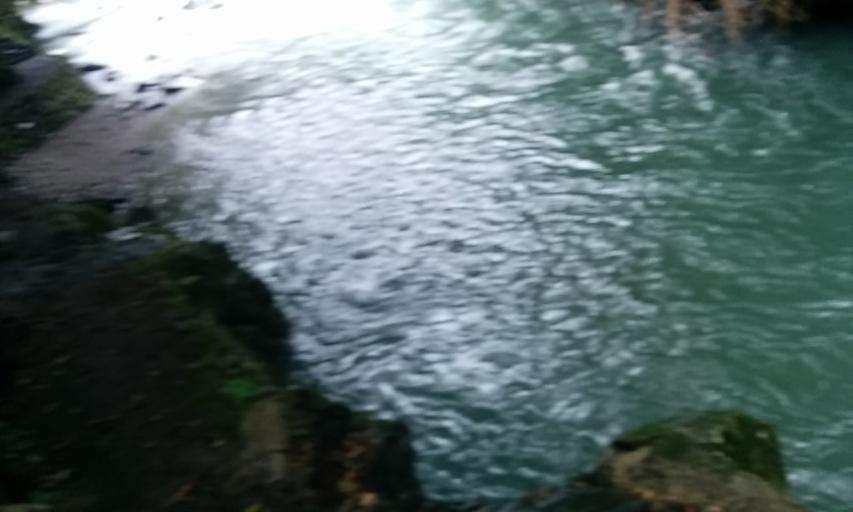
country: JP
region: Kyoto
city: Kameoka
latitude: 35.0474
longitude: 135.6609
